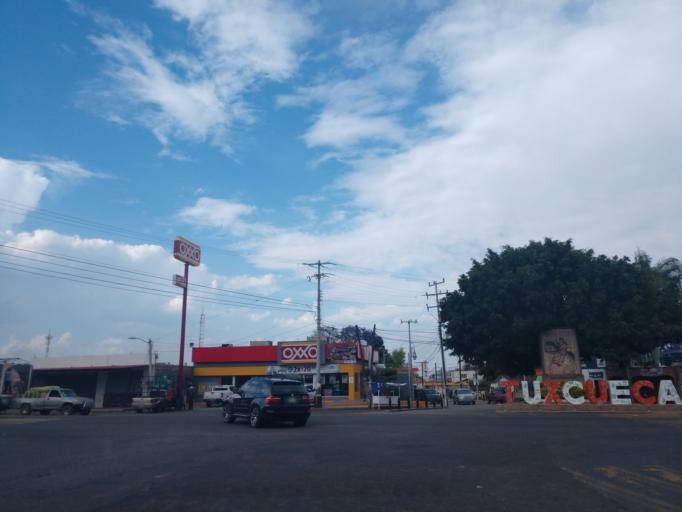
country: MX
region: Jalisco
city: Tizapan el Alto
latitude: 20.1527
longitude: -103.1860
